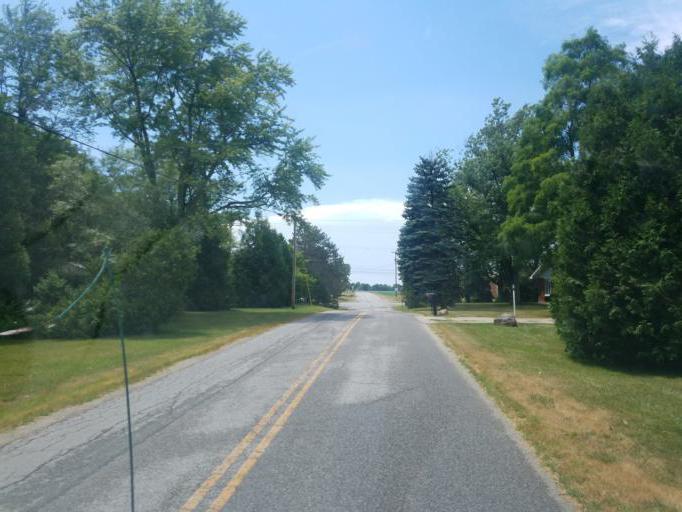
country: US
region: Ohio
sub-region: Paulding County
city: Antwerp
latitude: 41.1995
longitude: -84.7458
